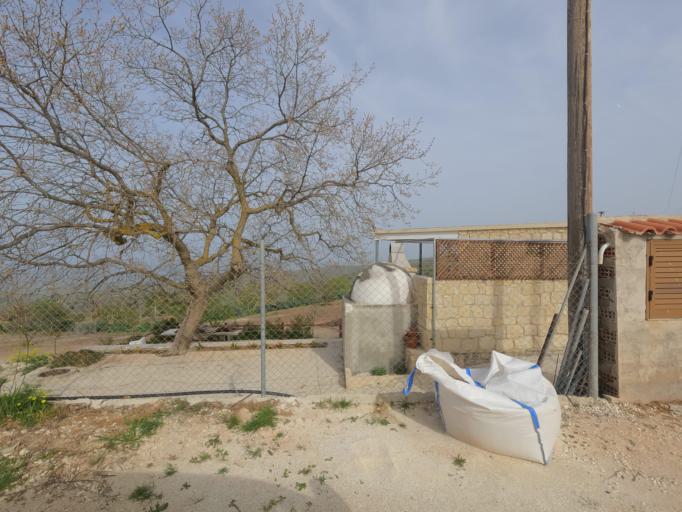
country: CY
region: Pafos
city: Pegeia
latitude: 34.9489
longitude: 32.3794
